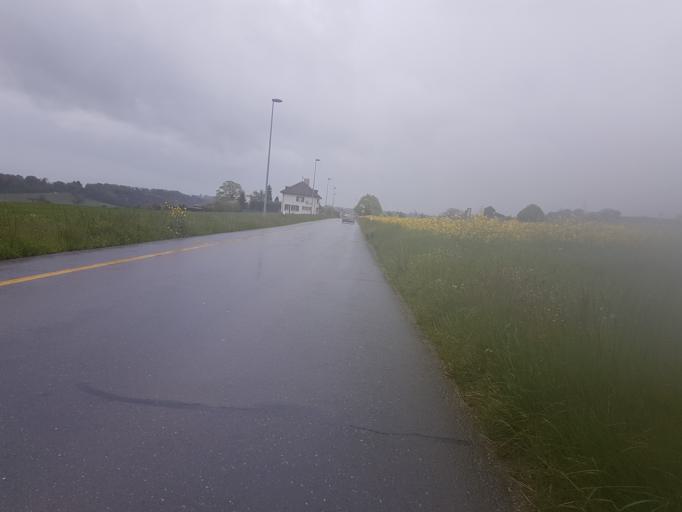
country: CH
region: Vaud
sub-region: Gros-de-Vaud District
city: Penthalaz
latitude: 46.6344
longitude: 6.5276
